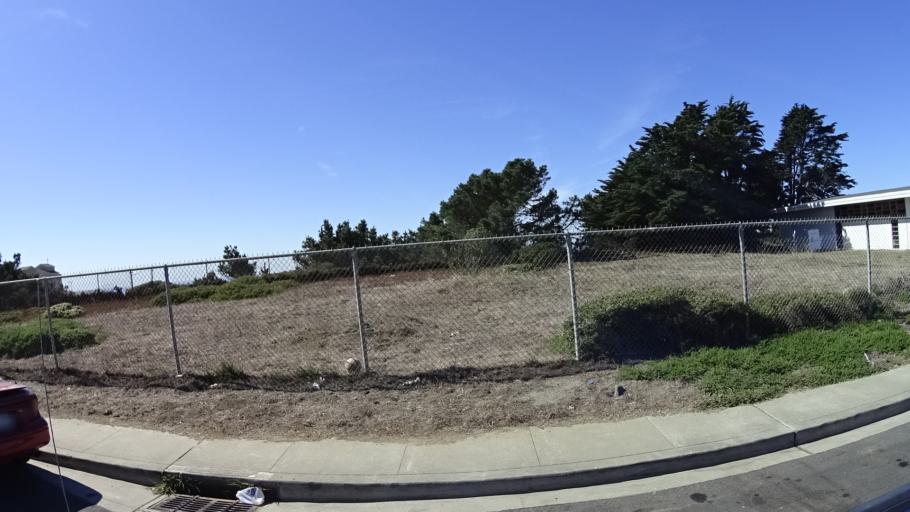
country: US
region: California
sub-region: San Mateo County
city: Broadmoor
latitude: 37.6820
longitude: -122.4912
